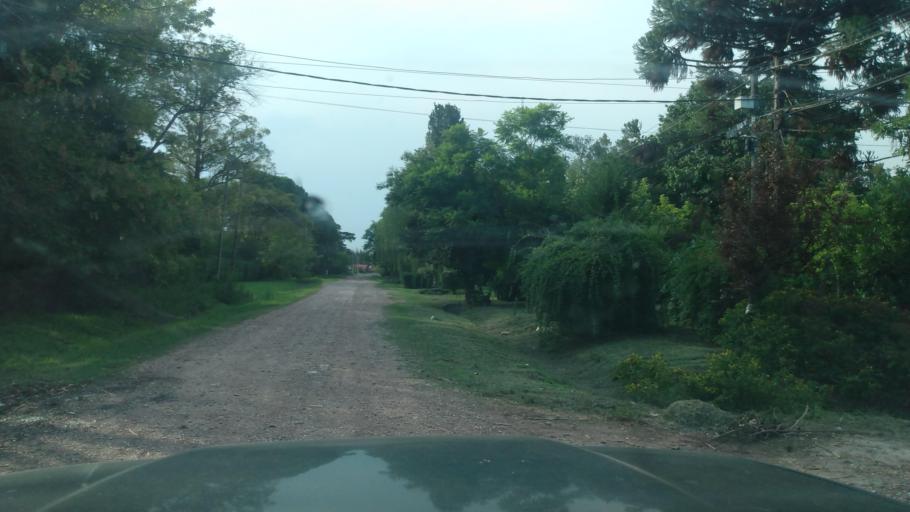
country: AR
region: Buenos Aires
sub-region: Partido de Lujan
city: Lujan
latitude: -34.5523
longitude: -59.1305
